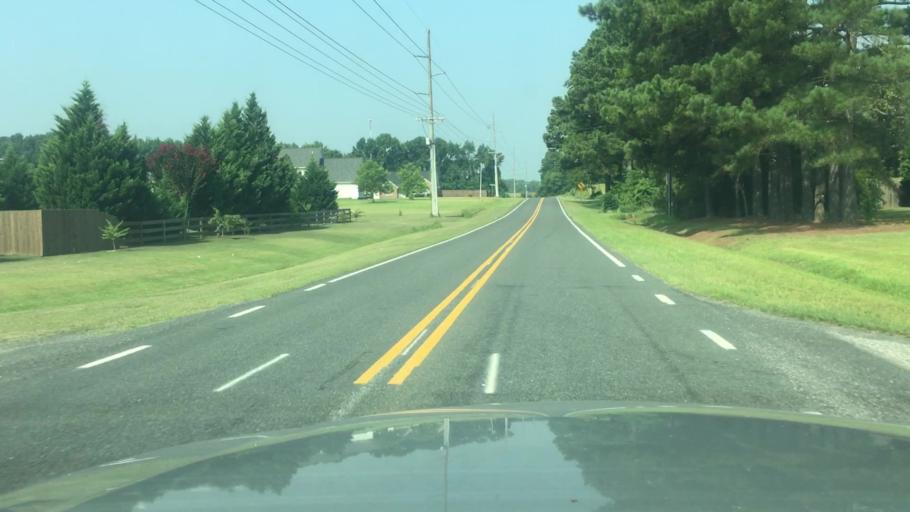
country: US
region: North Carolina
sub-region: Cumberland County
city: Hope Mills
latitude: 34.9005
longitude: -78.8796
